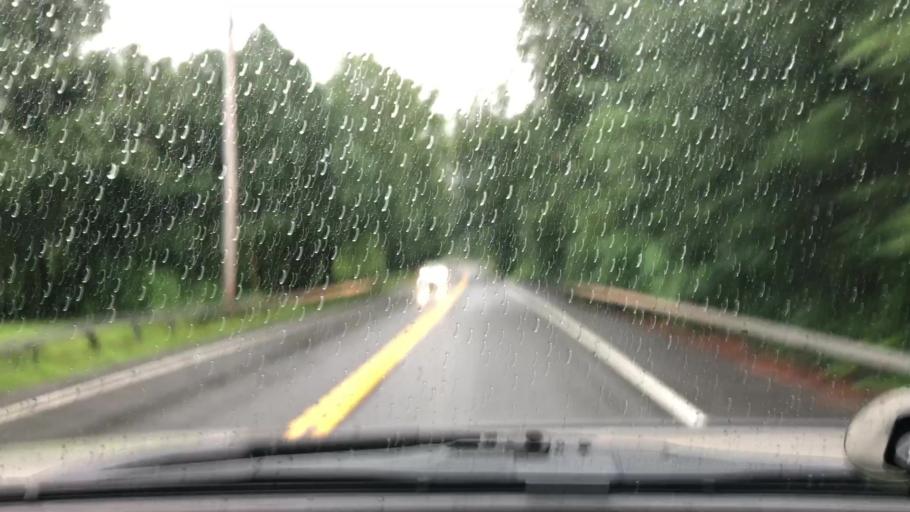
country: US
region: New York
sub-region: Greene County
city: Palenville
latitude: 42.1614
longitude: -73.9917
